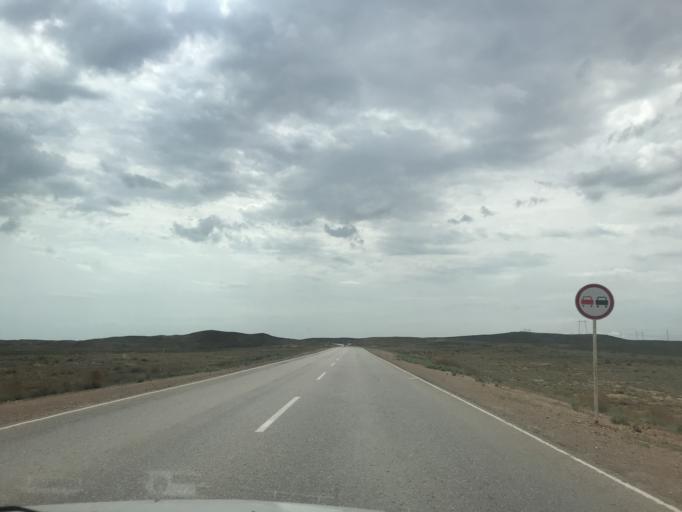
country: KZ
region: Zhambyl
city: Mynaral
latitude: 45.5163
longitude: 73.4926
